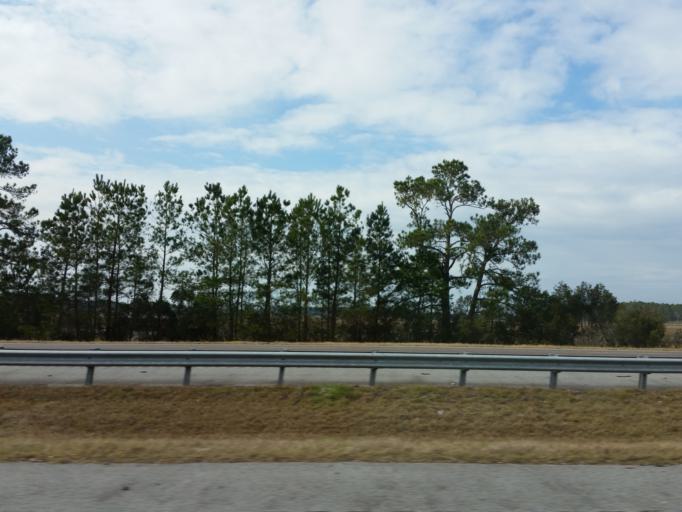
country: US
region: Georgia
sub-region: Liberty County
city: Midway
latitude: 31.8350
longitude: -81.3519
